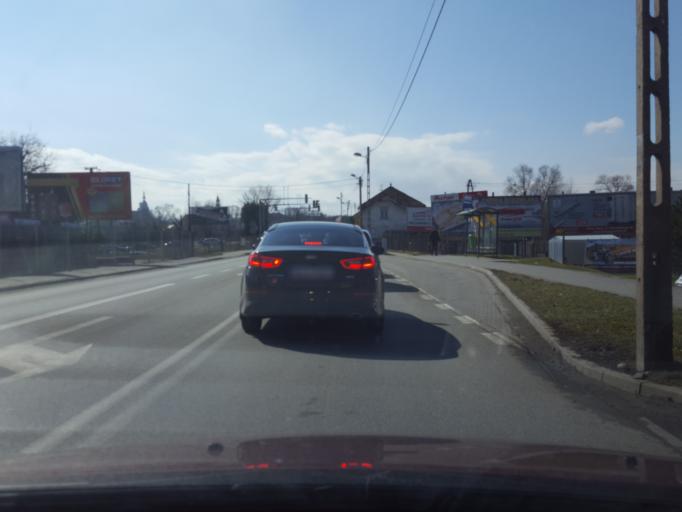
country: PL
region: Lesser Poland Voivodeship
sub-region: Powiat nowosadecki
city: Nowy Sacz
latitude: 49.6322
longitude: 20.6918
